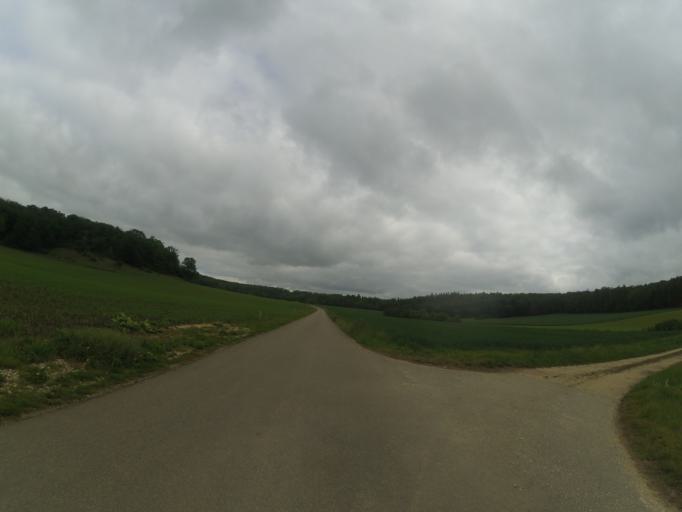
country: DE
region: Baden-Wuerttemberg
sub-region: Tuebingen Region
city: Bernstadt
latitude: 48.5121
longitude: 10.0320
